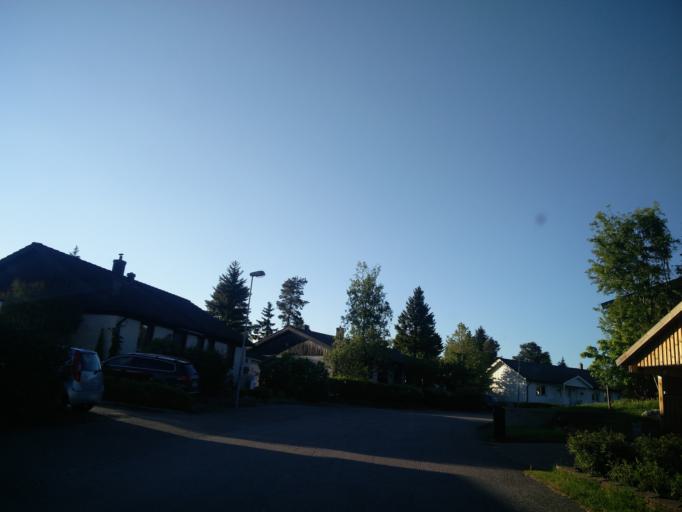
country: SE
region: Vaesternorrland
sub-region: Sundsvalls Kommun
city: Sundsvall
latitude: 62.4068
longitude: 17.2772
